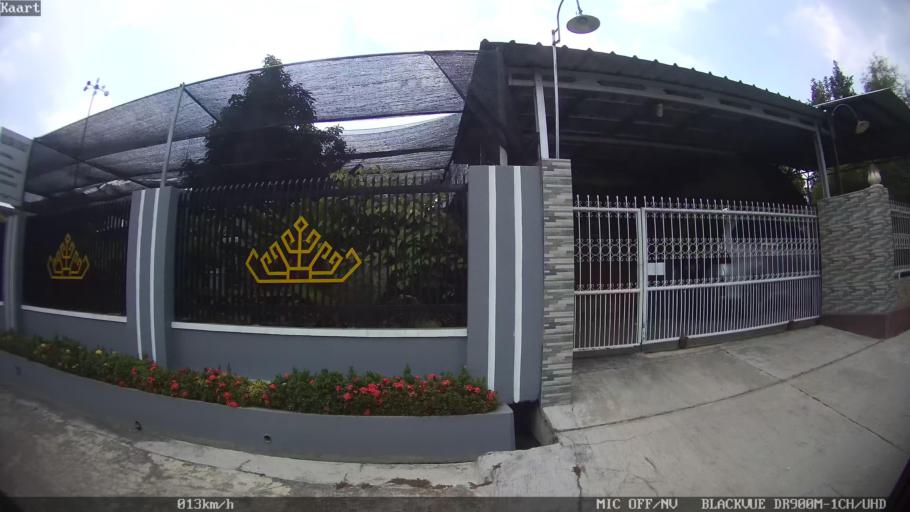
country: ID
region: Lampung
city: Pringsewu
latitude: -5.3446
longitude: 104.9784
